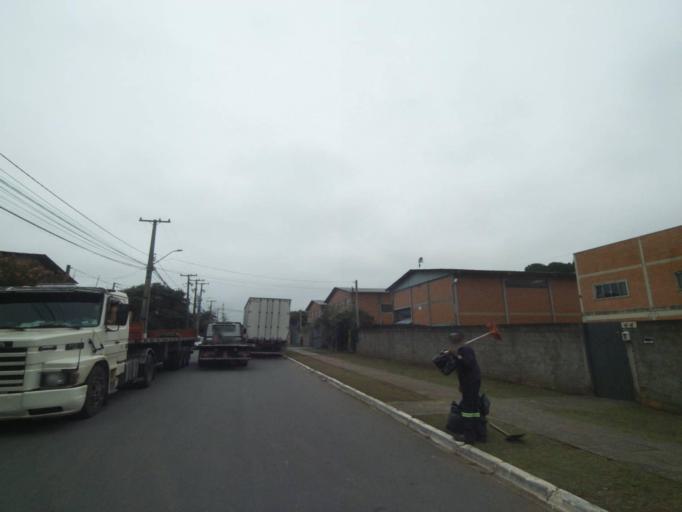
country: BR
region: Parana
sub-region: Araucaria
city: Araucaria
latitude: -25.5476
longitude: -49.3312
